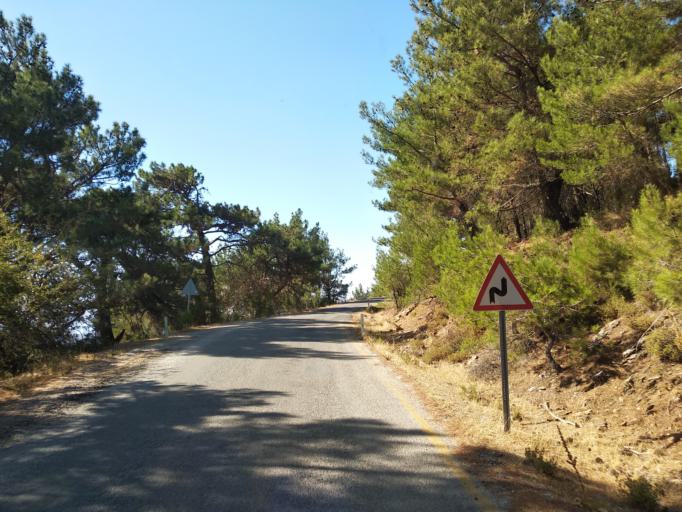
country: TR
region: Izmir
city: Gaziemir
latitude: 38.3086
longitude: 26.9986
